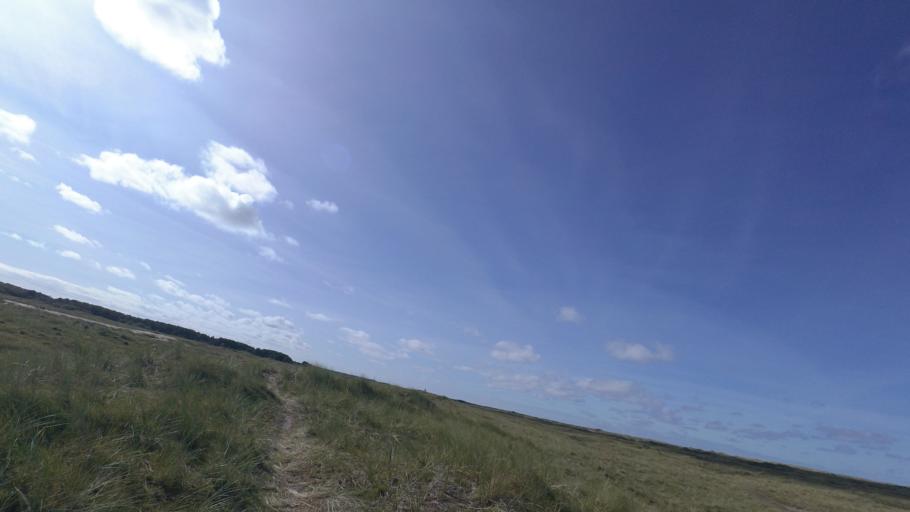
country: NL
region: Friesland
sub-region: Gemeente Ameland
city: Hollum
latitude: 53.4549
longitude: 5.7047
